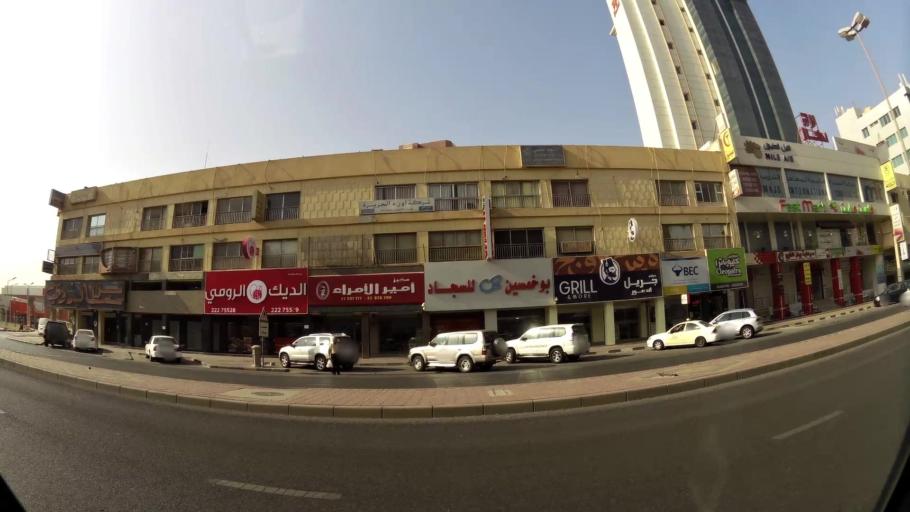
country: KW
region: Muhafazat Hawalli
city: Hawalli
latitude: 29.3411
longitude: 48.0200
